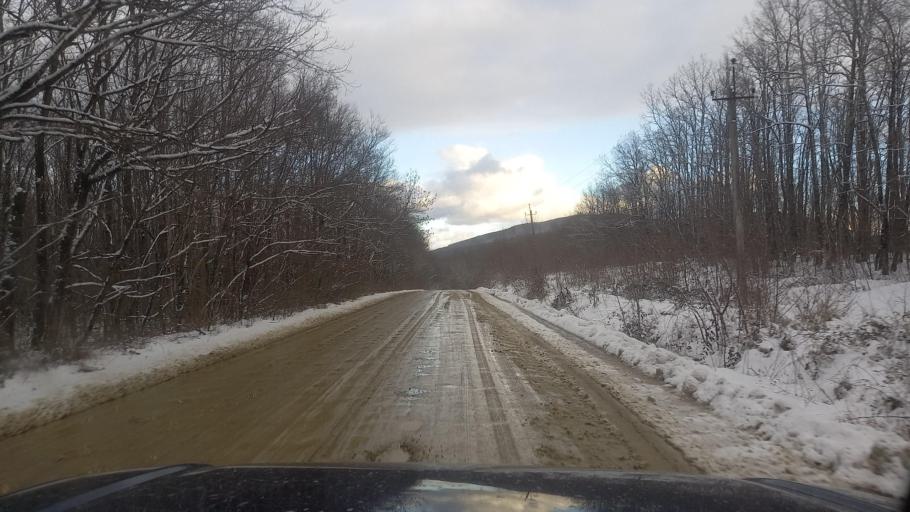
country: RU
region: Krasnodarskiy
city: Smolenskaya
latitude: 44.6759
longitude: 38.7336
